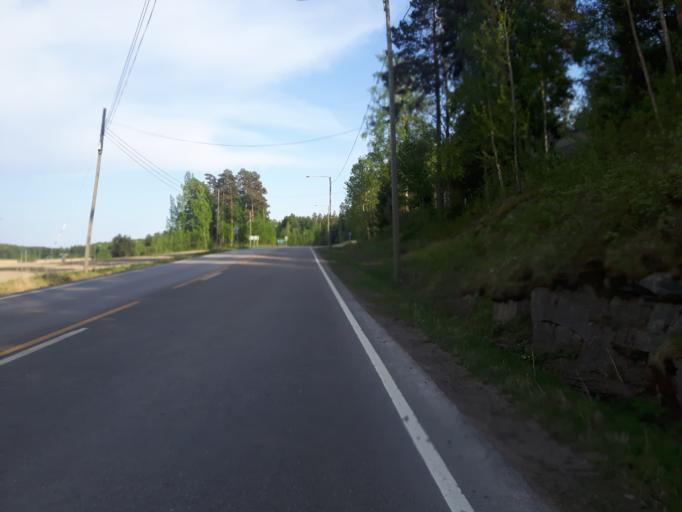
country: FI
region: Uusimaa
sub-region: Loviisa
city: Perna
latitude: 60.4998
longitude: 25.9558
